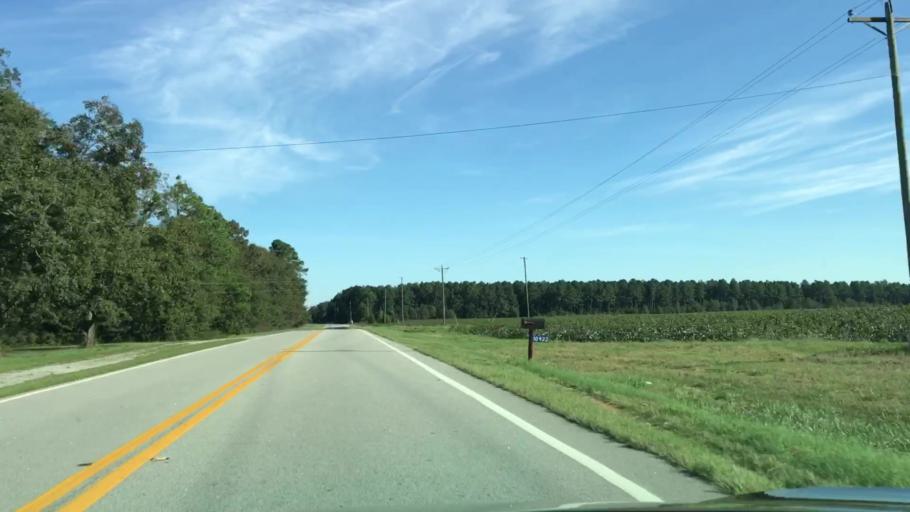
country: US
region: Georgia
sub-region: Glascock County
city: Gibson
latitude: 33.3135
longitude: -82.5418
